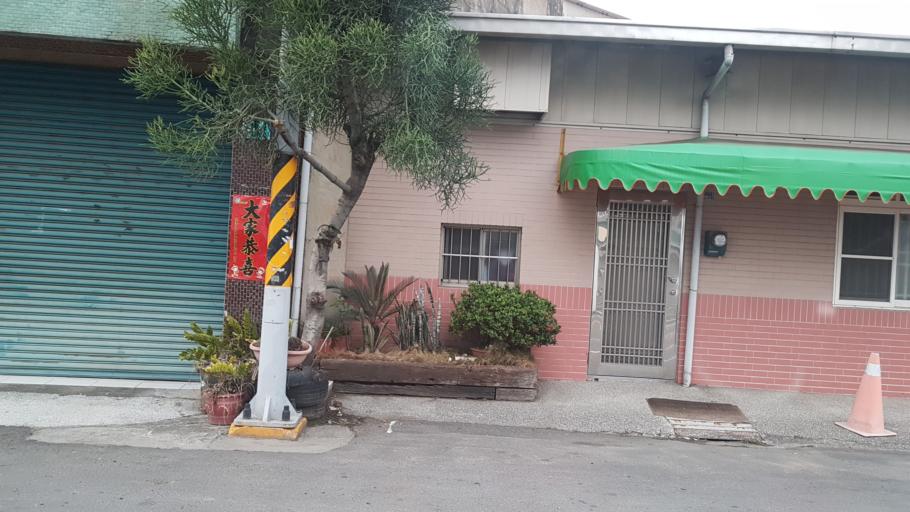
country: TW
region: Taiwan
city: Xinying
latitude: 23.3299
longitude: 120.3164
